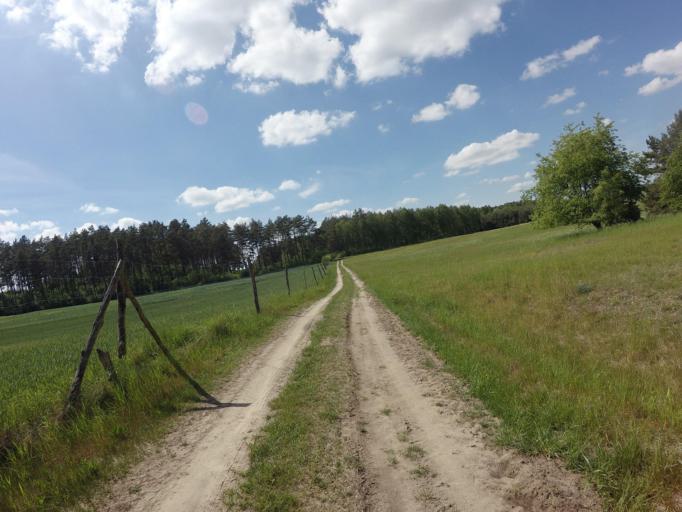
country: PL
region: West Pomeranian Voivodeship
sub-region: Powiat choszczenski
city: Recz
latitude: 53.2206
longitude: 15.5218
